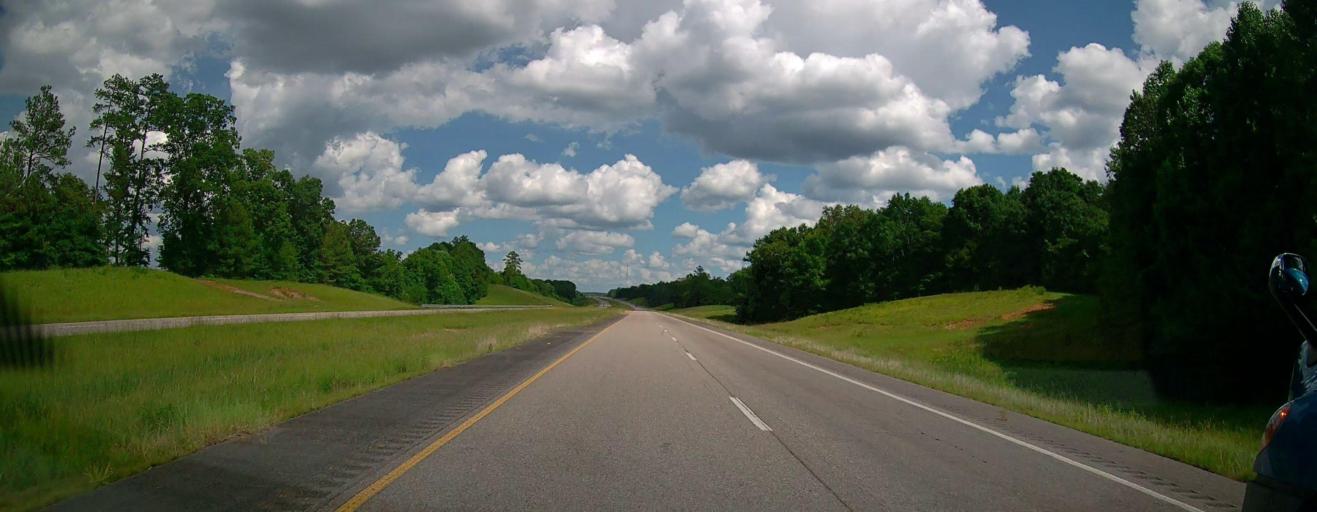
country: US
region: Mississippi
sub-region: Lowndes County
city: New Hope
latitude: 33.4840
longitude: -88.2636
